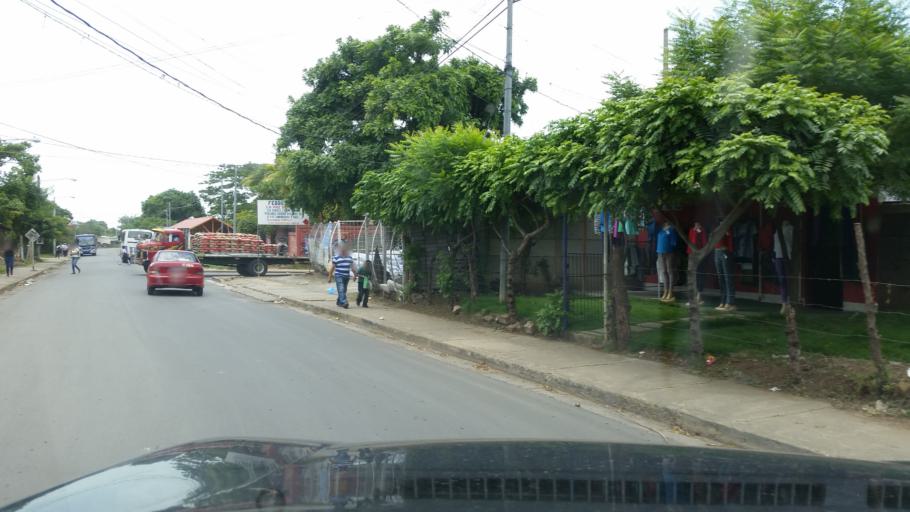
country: NI
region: Managua
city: Managua
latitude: 12.1349
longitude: -86.2089
